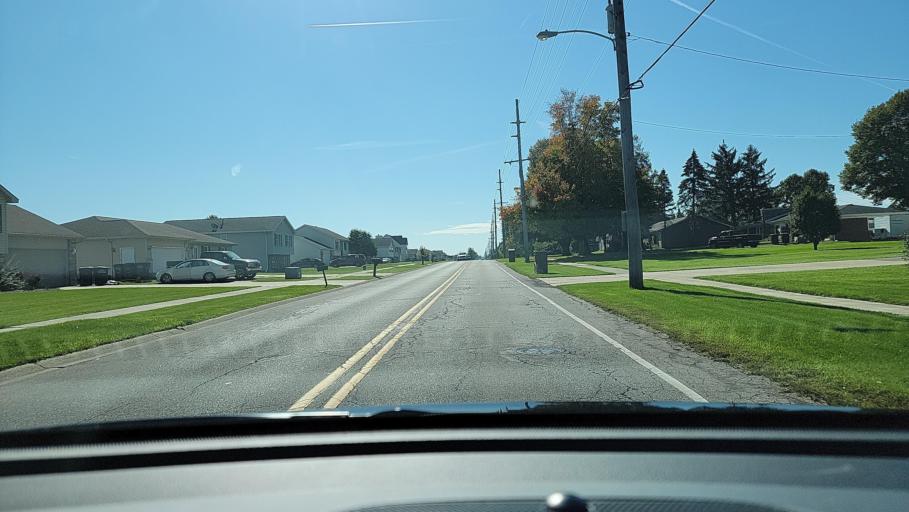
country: US
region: Indiana
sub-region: Porter County
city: Portage
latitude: 41.5679
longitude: -87.1636
